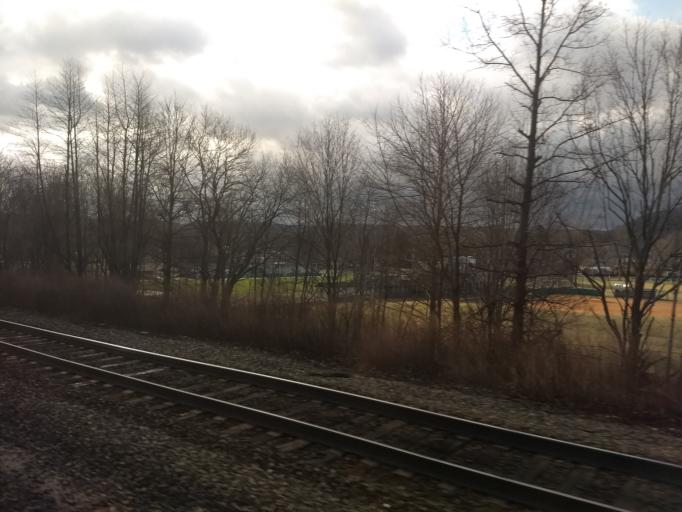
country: US
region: Pennsylvania
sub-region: Cambria County
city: Portage
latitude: 40.3888
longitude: -78.6860
